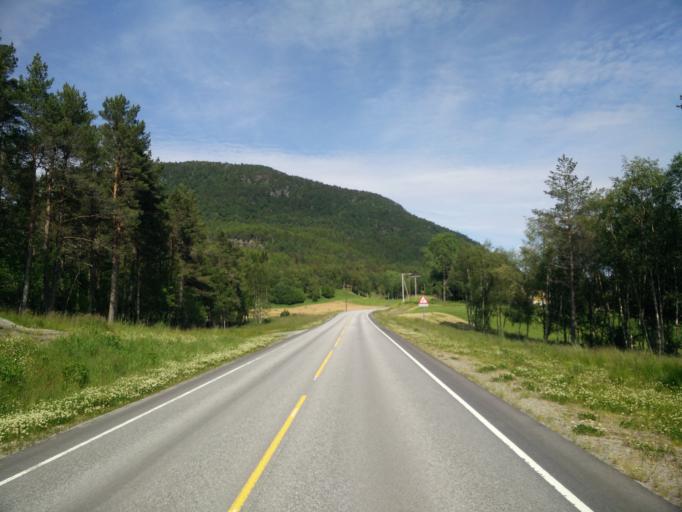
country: NO
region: More og Romsdal
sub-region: Tingvoll
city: Tingvoll
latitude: 63.0474
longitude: 8.0757
